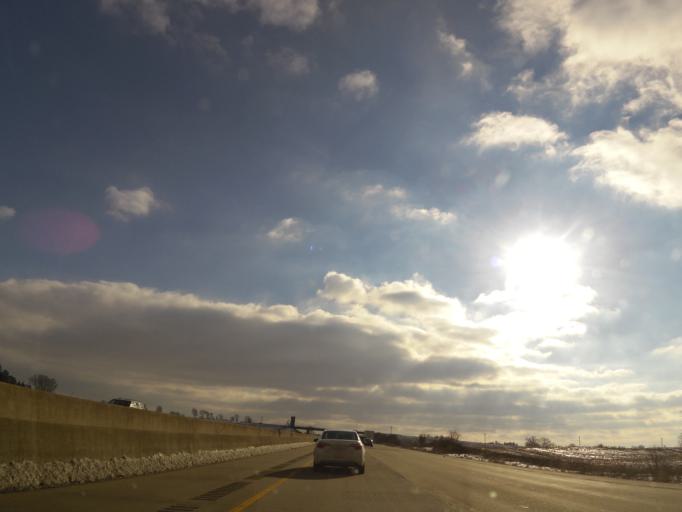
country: US
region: Wisconsin
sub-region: Columbia County
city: Poynette
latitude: 43.3558
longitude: -89.4596
